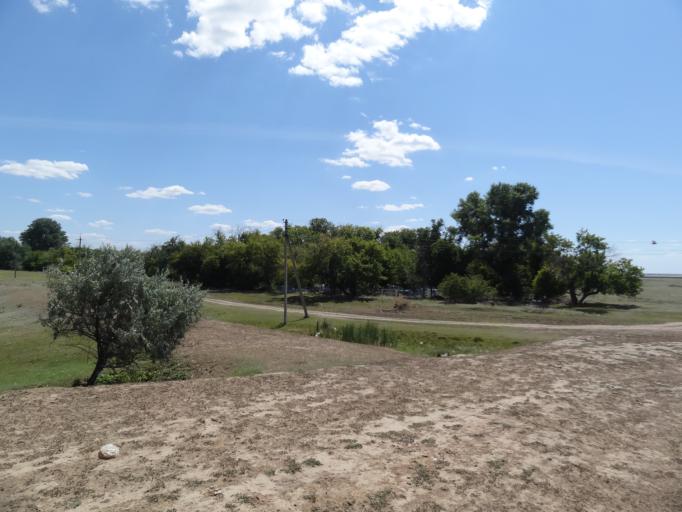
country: RU
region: Saratov
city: Sovetskoye
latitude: 51.2879
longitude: 46.6548
